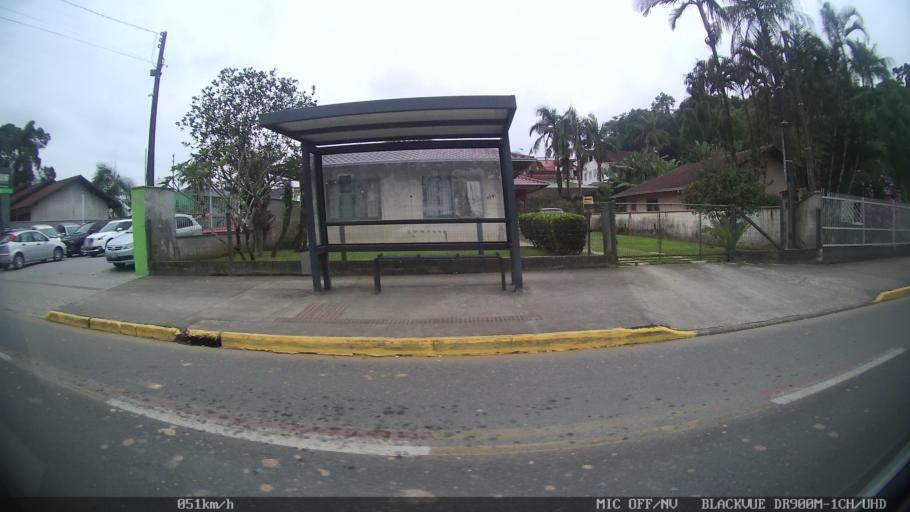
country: BR
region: Santa Catarina
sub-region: Joinville
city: Joinville
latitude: -26.3415
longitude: -48.8422
